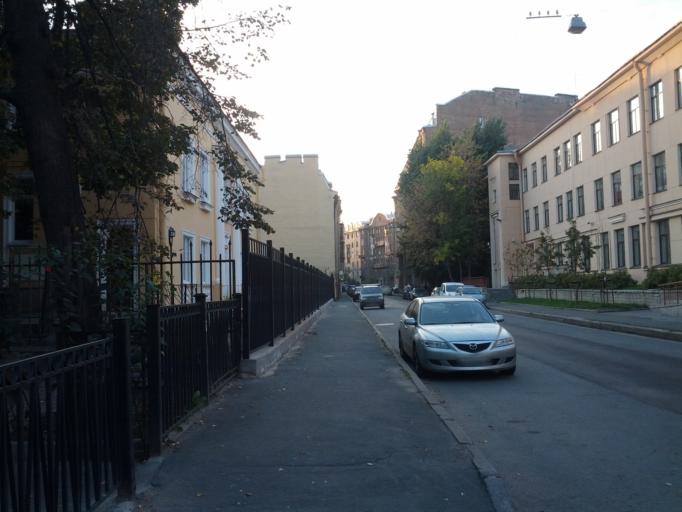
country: RU
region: St.-Petersburg
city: Petrogradka
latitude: 59.9534
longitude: 30.3050
